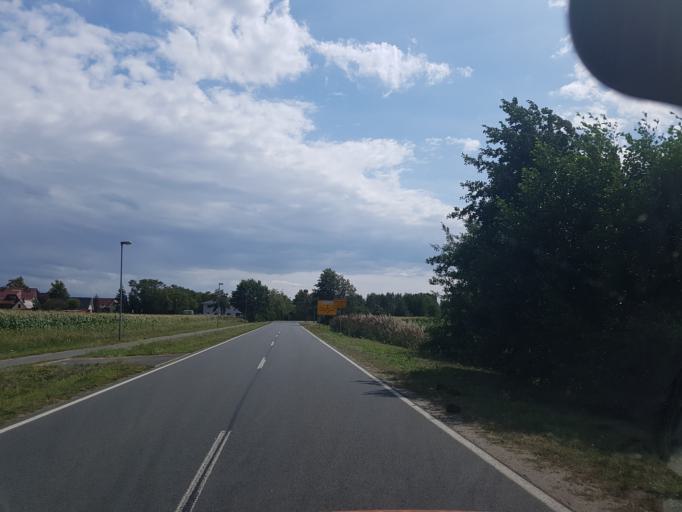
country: DE
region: Brandenburg
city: Herzberg
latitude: 51.6828
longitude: 13.2049
